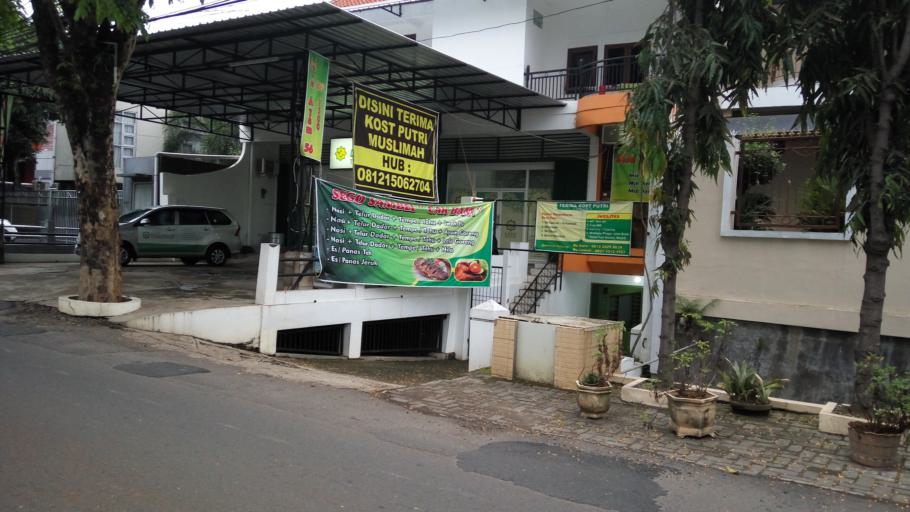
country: ID
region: Central Java
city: Semarang
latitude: -7.0550
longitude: 110.4325
